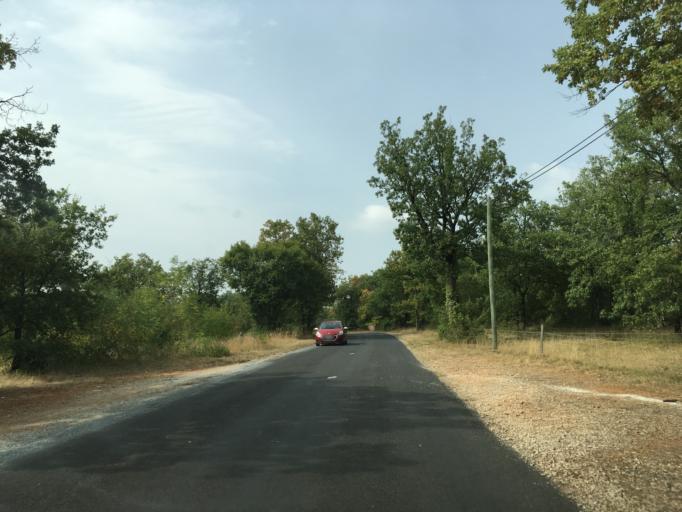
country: FR
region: Midi-Pyrenees
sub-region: Departement du Lot
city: Gramat
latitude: 44.8232
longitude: 1.6004
